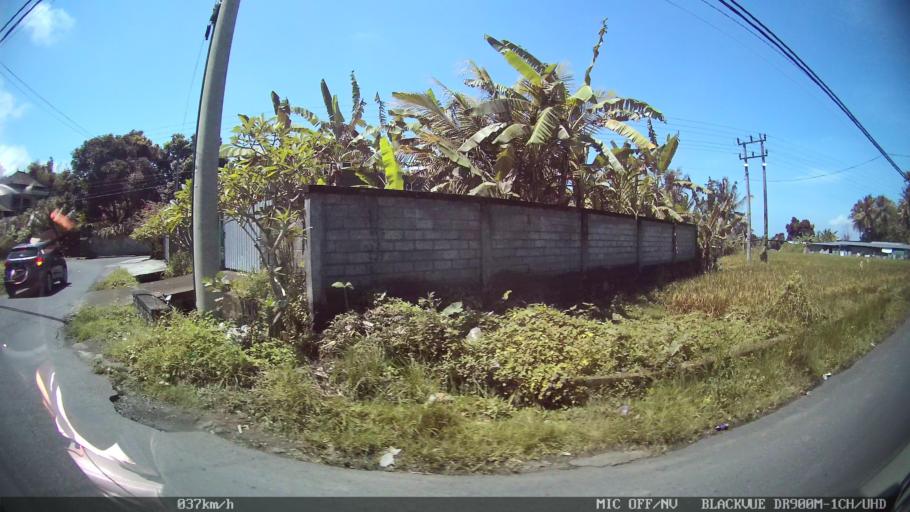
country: ID
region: Bali
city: Banjar Kelodan
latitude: -8.5554
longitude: 115.3363
